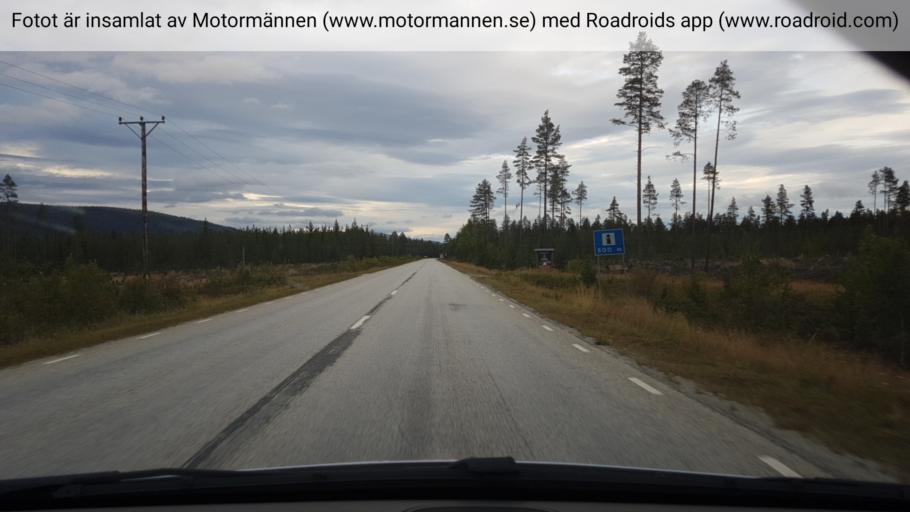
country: SE
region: Jaemtland
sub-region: Bergs Kommun
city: Hoverberg
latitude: 62.4988
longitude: 14.2080
